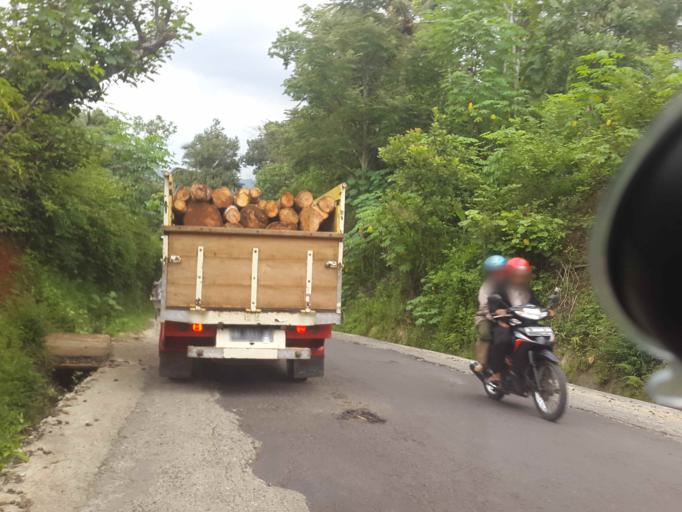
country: ID
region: Central Java
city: Banyumas
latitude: -7.5348
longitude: 109.3140
